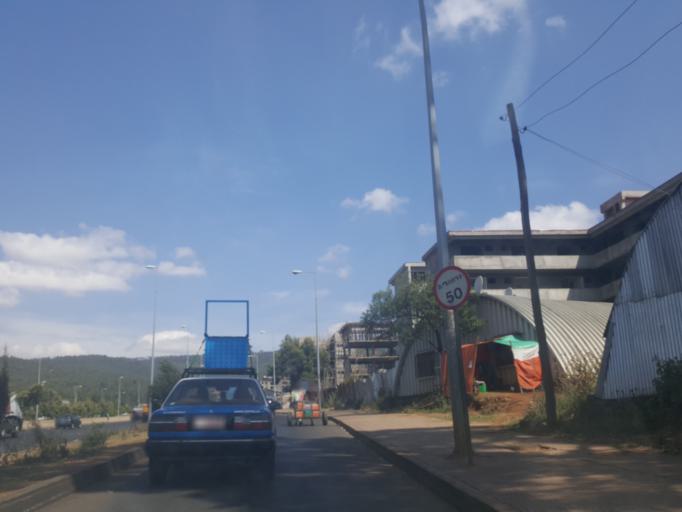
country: ET
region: Adis Abeba
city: Addis Ababa
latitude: 9.0623
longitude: 38.7149
